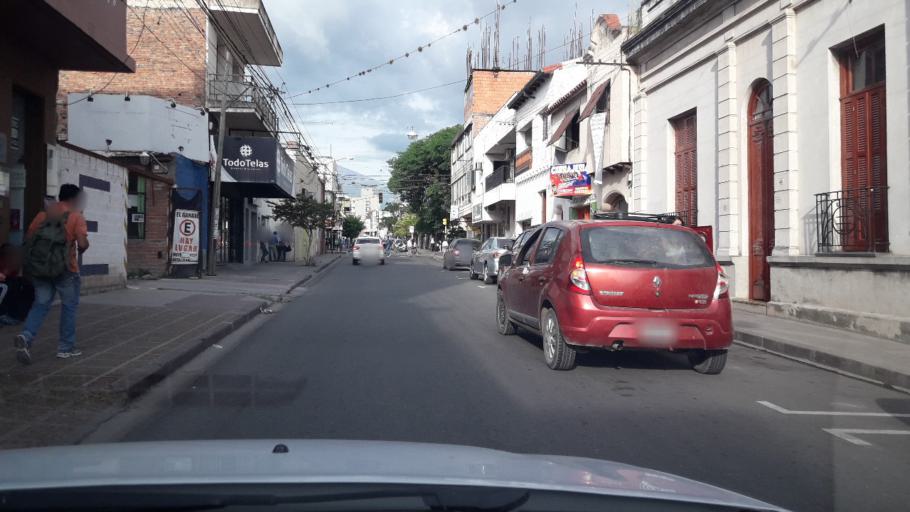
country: AR
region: Jujuy
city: San Salvador de Jujuy
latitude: -24.1878
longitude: -65.3020
